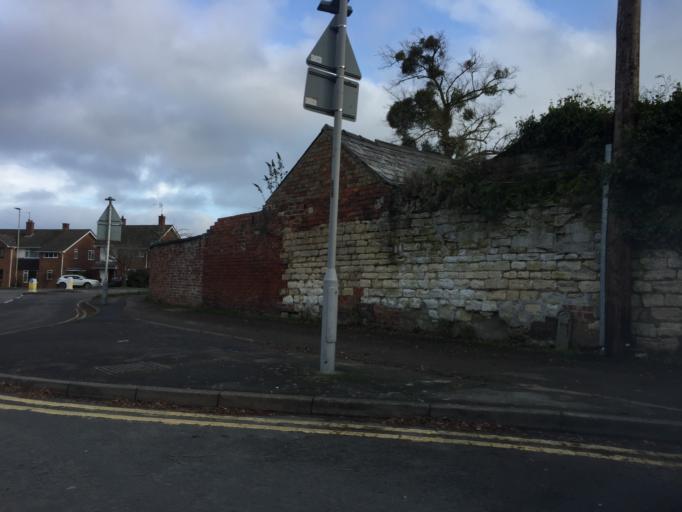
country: GB
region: England
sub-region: Gloucestershire
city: Cheltenham
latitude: 51.8800
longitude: -2.0783
